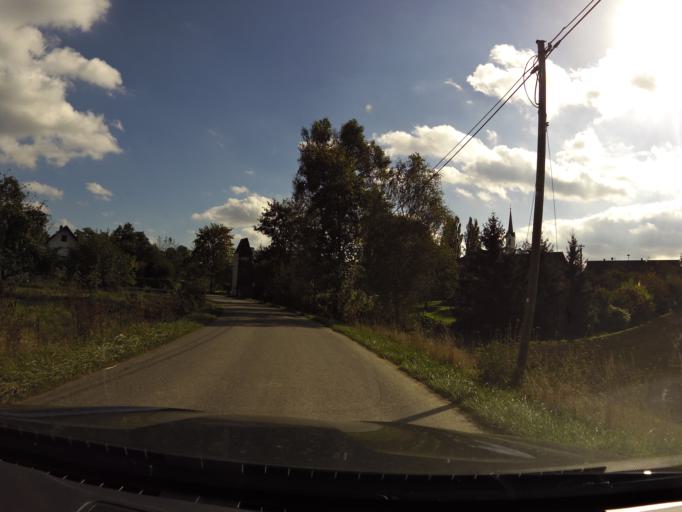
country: DE
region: Bavaria
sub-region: Lower Bavaria
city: Vilsheim
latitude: 48.4297
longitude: 12.1262
